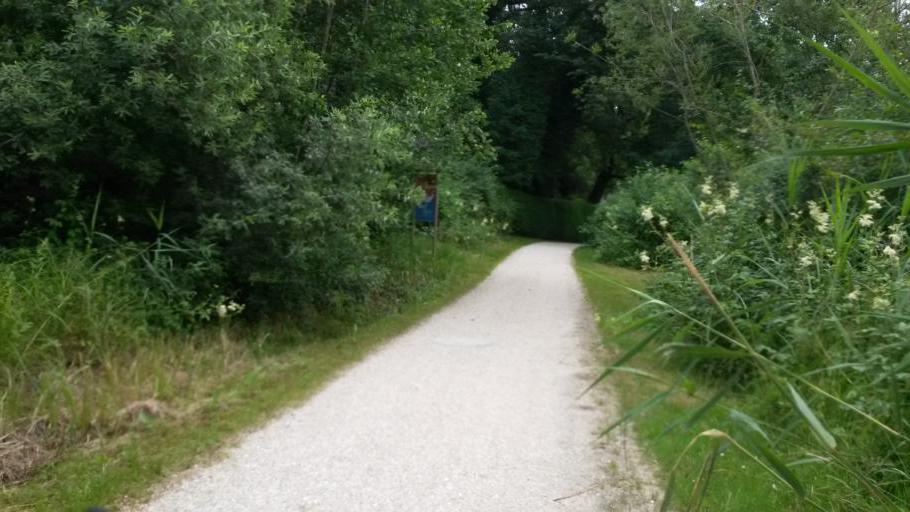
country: DE
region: Bavaria
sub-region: Upper Bavaria
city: Gstadt am Chiemsee
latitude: 47.8863
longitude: 12.3842
